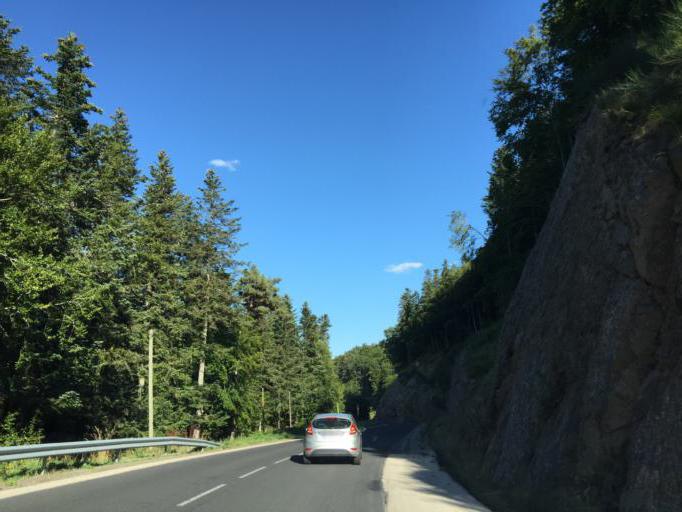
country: FR
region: Auvergne
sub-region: Departement de la Haute-Loire
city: Saugues
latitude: 44.9817
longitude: 3.6188
